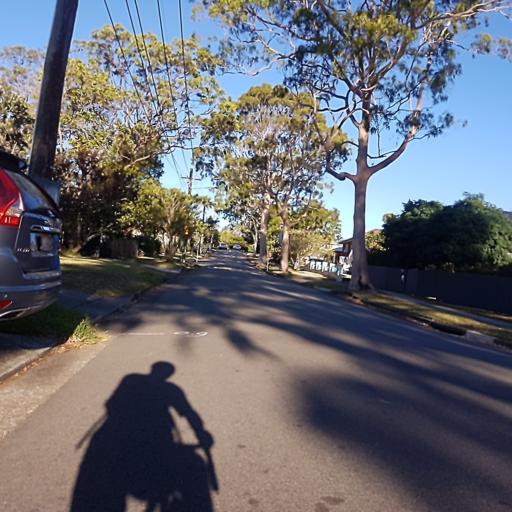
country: AU
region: New South Wales
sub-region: Warringah
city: Forestville
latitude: -33.7553
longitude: 151.2182
